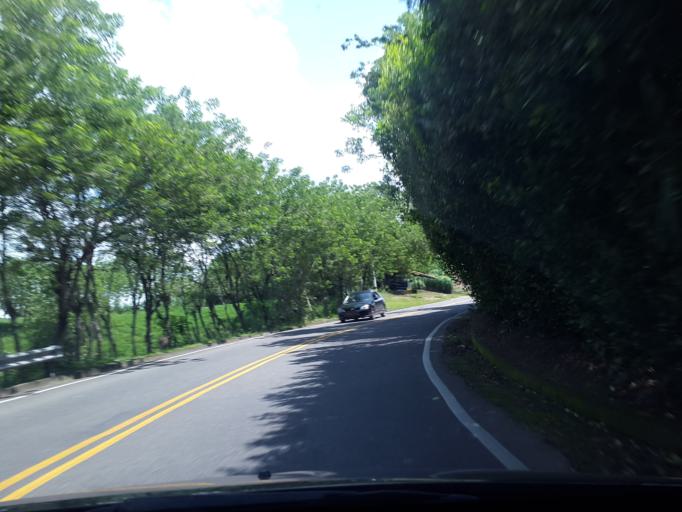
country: CO
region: Valle del Cauca
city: Alcala
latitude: 4.6874
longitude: -75.8148
